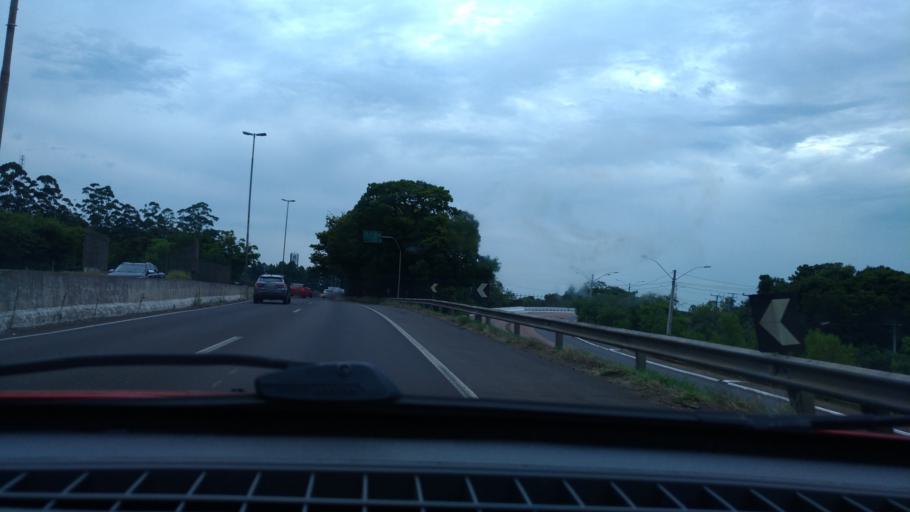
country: BR
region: Rio Grande do Sul
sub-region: Esteio
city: Esteio
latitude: -29.8700
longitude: -51.1802
